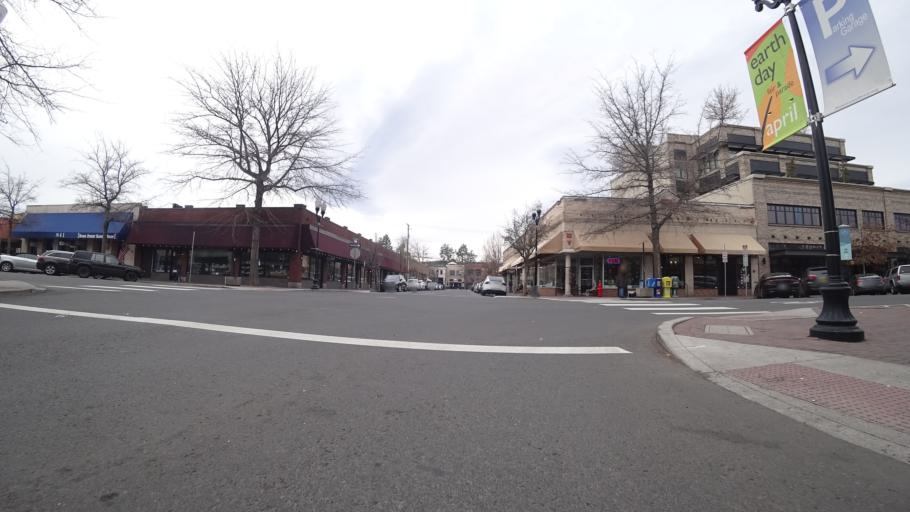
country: US
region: Oregon
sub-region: Deschutes County
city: Bend
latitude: 44.0581
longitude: -121.3130
